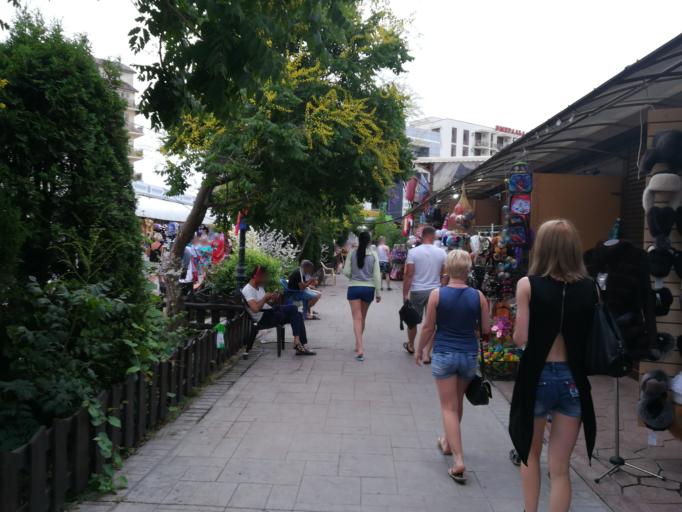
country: RU
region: Krasnodarskiy
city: Vityazevo
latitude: 44.9866
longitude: 37.2552
